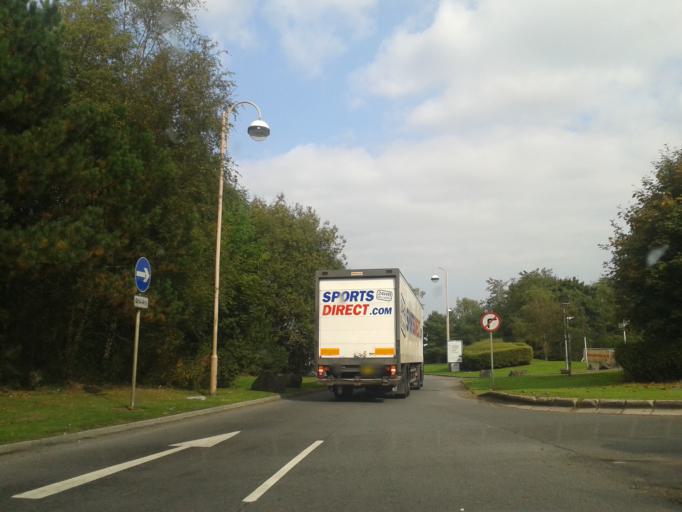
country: GB
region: Scotland
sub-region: Dumfries and Galloway
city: Lochmaben
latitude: 55.2184
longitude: -3.4116
